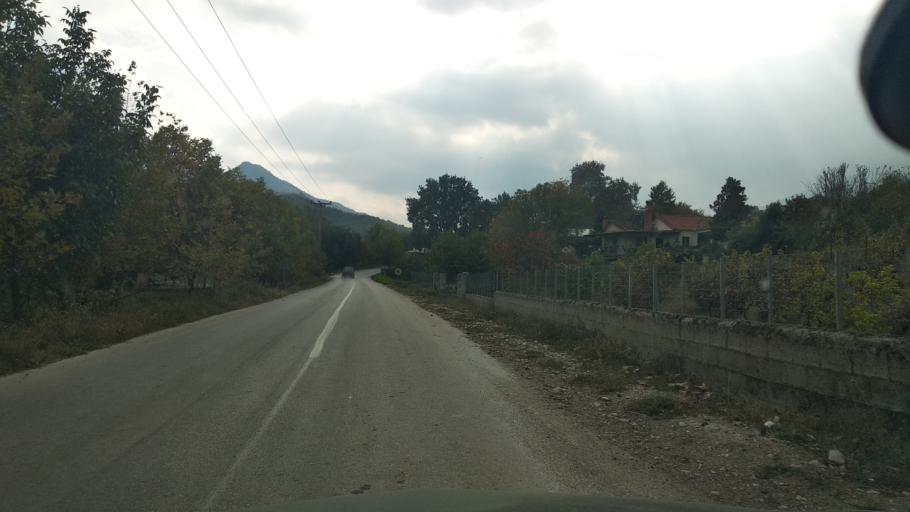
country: GR
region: Thessaly
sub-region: Trikala
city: Kastraki
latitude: 39.6956
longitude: 21.5217
